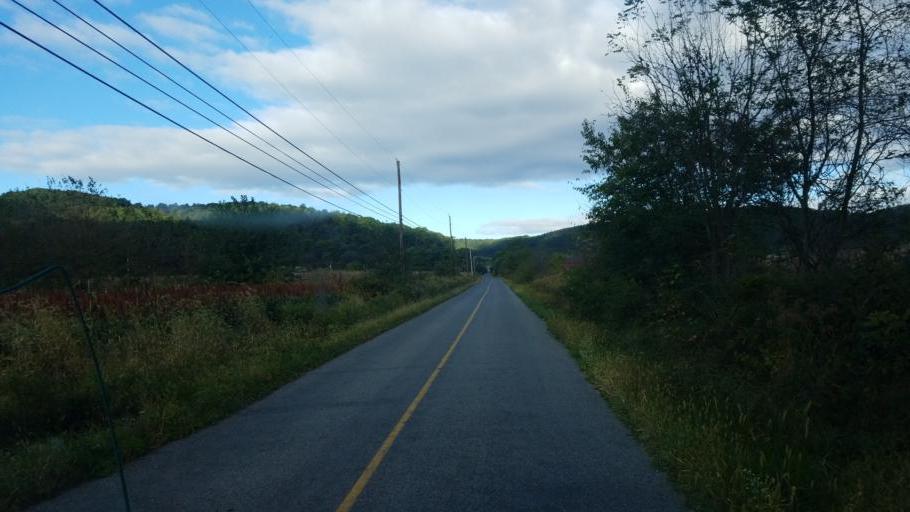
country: US
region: Pennsylvania
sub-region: Adams County
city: Biglerville
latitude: 39.8906
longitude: -77.3507
